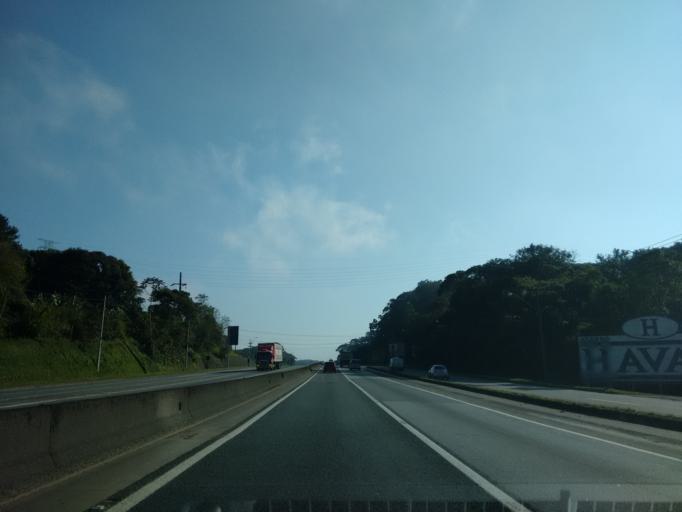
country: BR
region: Santa Catarina
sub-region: Joinville
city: Joinville
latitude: -26.2939
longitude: -48.8844
